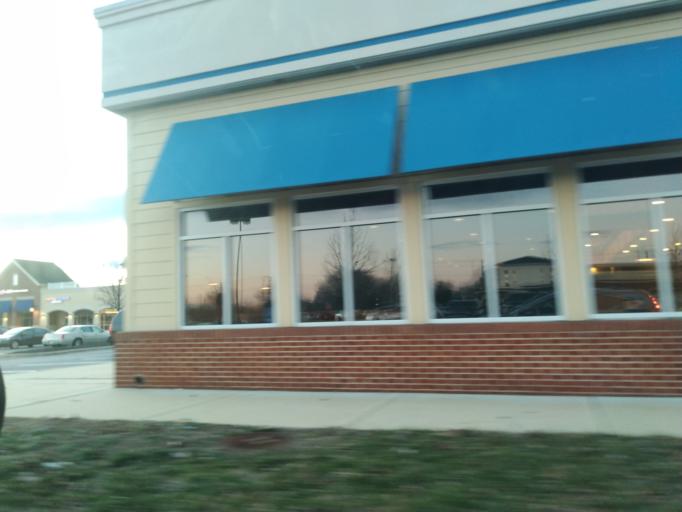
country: US
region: Maryland
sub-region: Anne Arundel County
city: Londontowne
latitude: 38.9444
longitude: -76.5621
